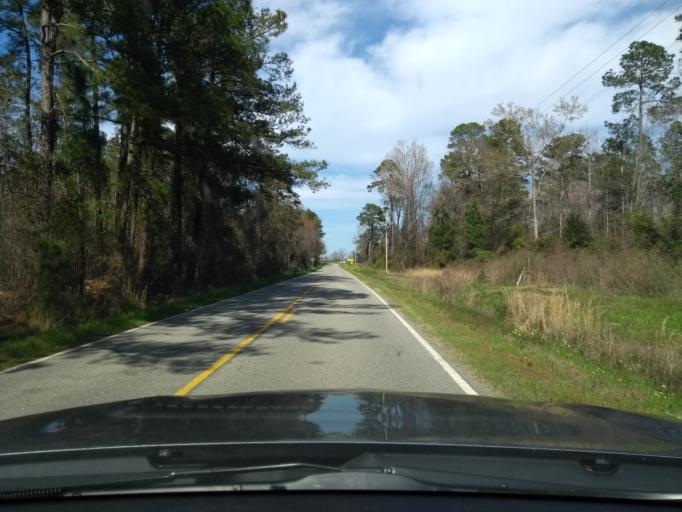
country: US
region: Georgia
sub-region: Bulloch County
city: Brooklet
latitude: 32.4517
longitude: -81.6626
